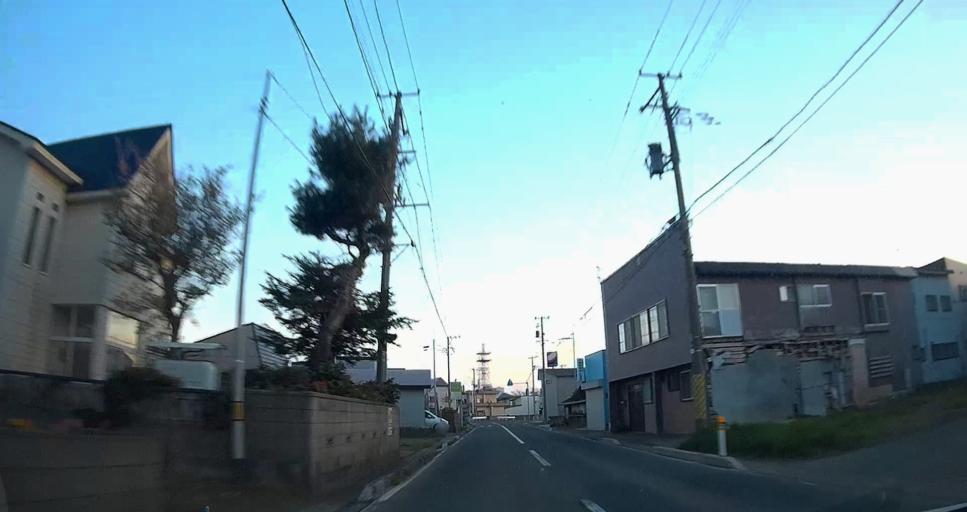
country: JP
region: Aomori
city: Misawa
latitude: 40.8688
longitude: 141.1306
